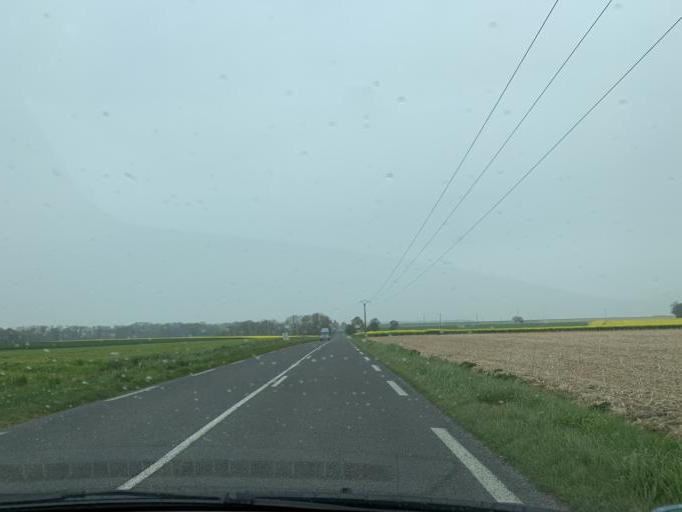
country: FR
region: Haute-Normandie
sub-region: Departement de la Seine-Maritime
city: Cany-Barville
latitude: 49.7979
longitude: 0.6644
